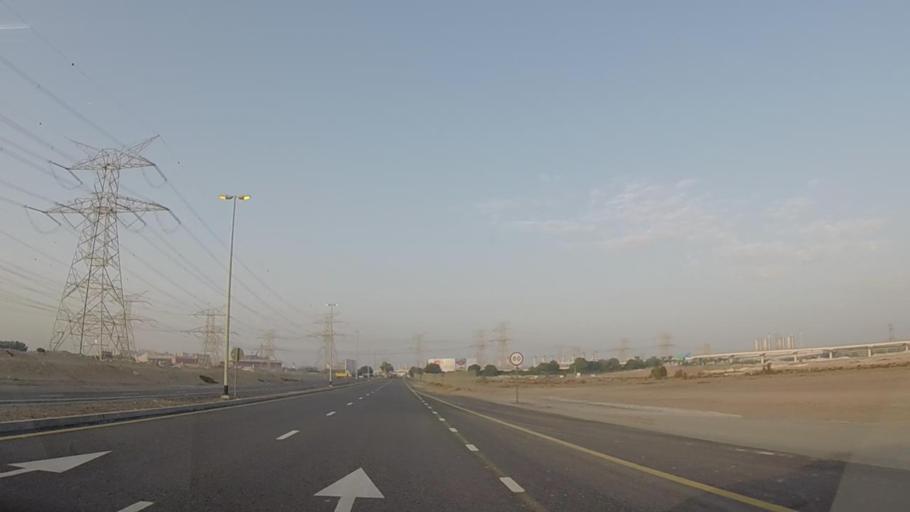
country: AE
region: Dubai
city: Dubai
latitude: 25.0523
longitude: 55.1257
